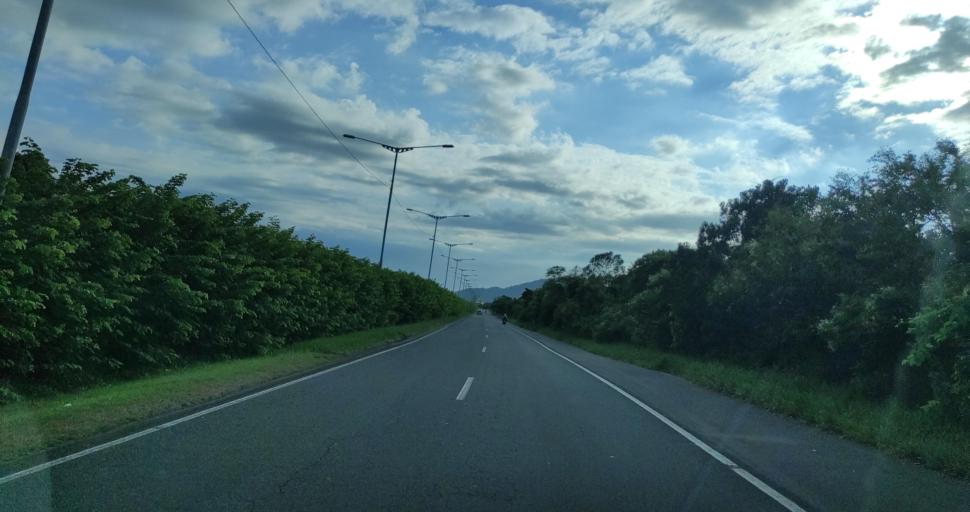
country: BR
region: Santa Catarina
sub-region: Penha
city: Penha
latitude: -26.8059
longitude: -48.6391
